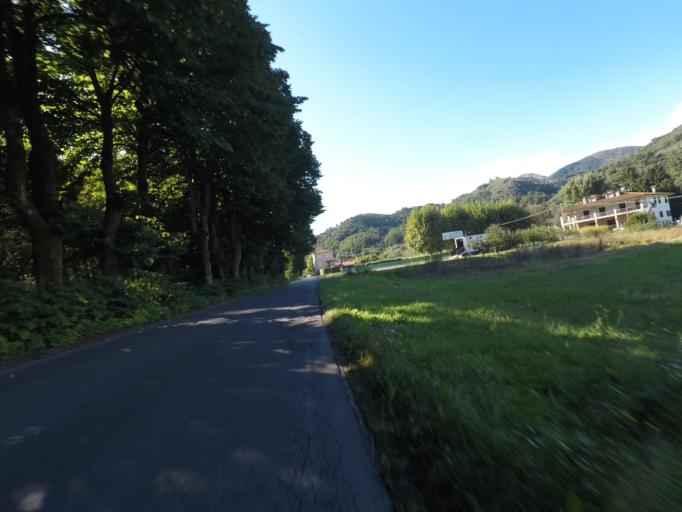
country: IT
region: Tuscany
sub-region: Provincia di Lucca
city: San Martino in Freddana-Monsagrati
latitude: 43.8988
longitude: 10.3887
